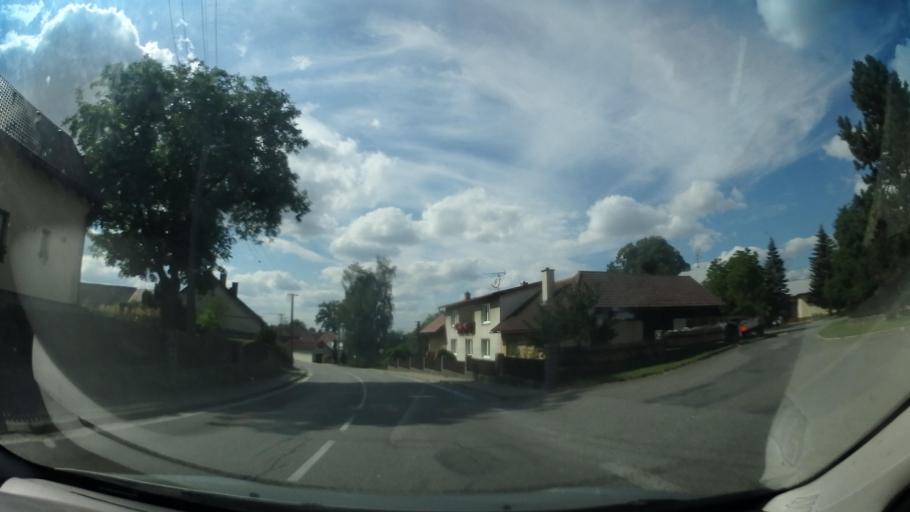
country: CZ
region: Vysocina
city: Pribyslav
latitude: 49.5645
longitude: 15.8110
